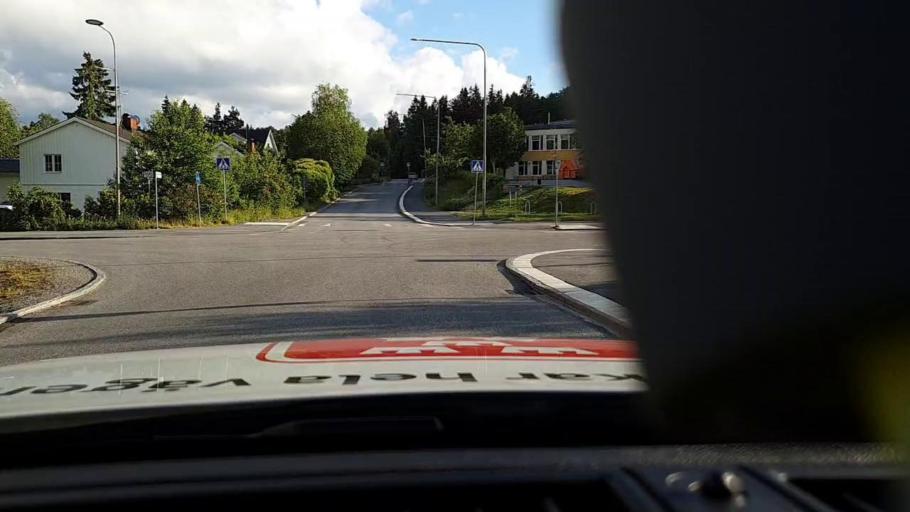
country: SE
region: Stockholm
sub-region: Huddinge Kommun
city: Huddinge
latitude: 59.2500
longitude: 17.9630
